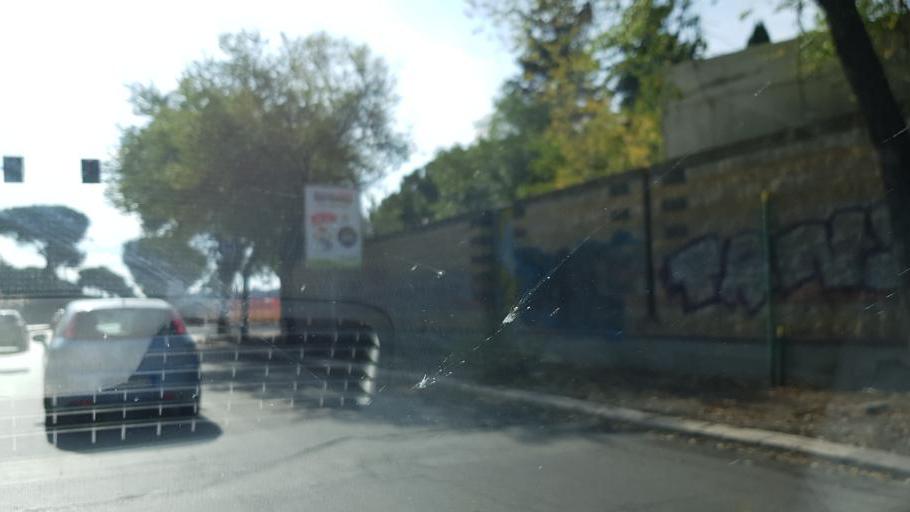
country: IT
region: Apulia
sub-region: Provincia di Foggia
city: Foggia
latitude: 41.4615
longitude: 15.5644
